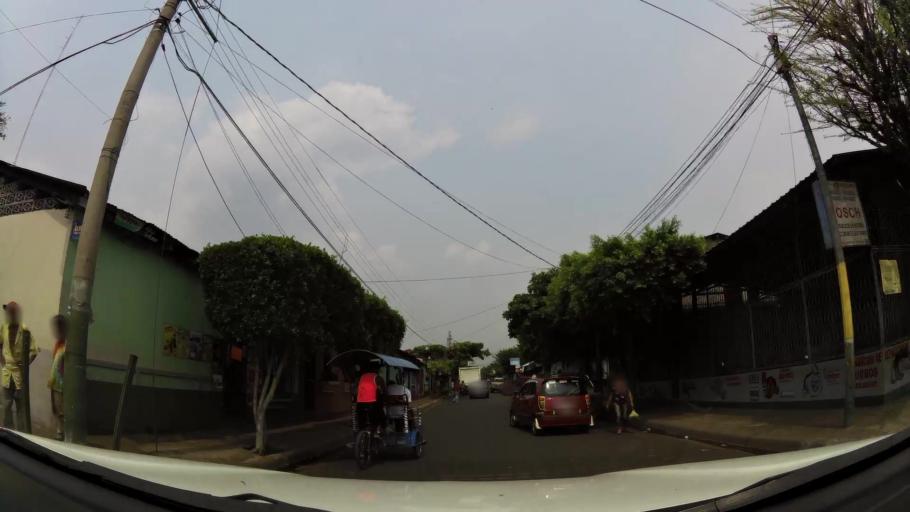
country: NI
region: Chinandega
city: Chinandega
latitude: 12.6265
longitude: -87.1273
